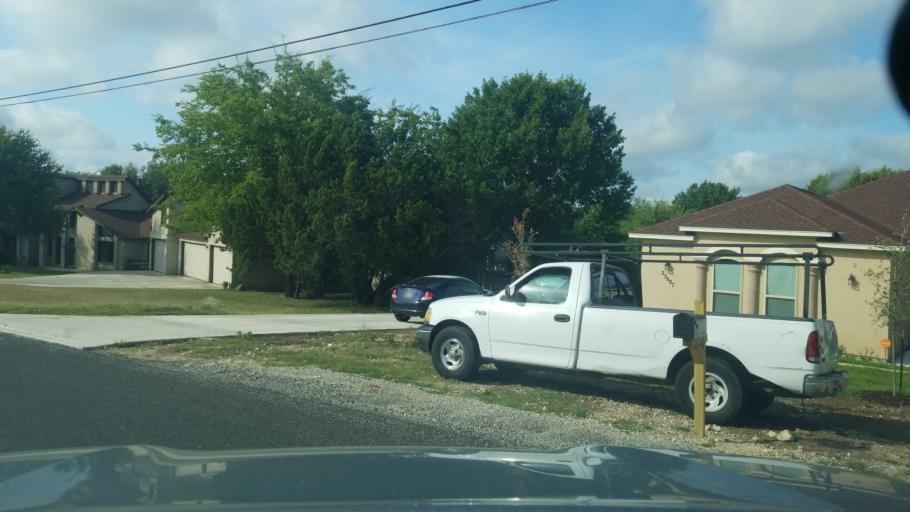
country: US
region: Texas
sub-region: Bexar County
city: Timberwood Park
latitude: 29.6824
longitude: -98.5075
